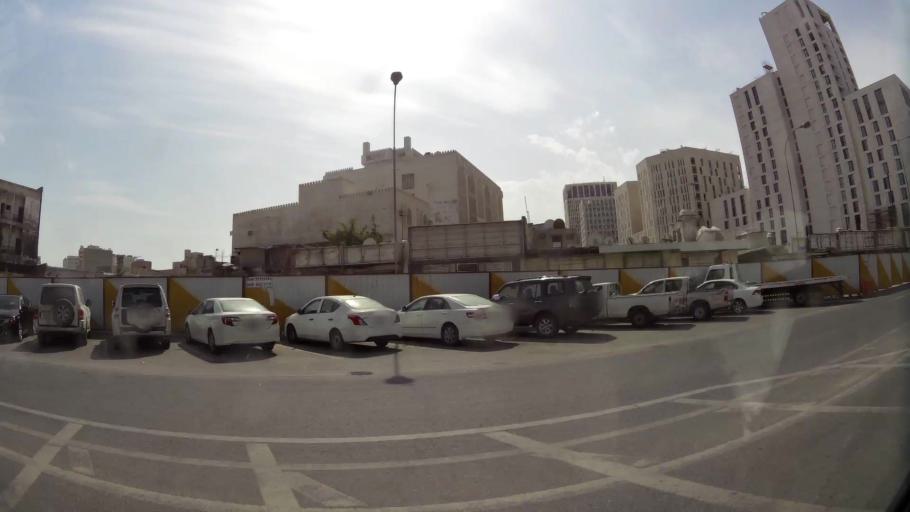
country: QA
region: Baladiyat ad Dawhah
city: Doha
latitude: 25.2849
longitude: 51.5316
